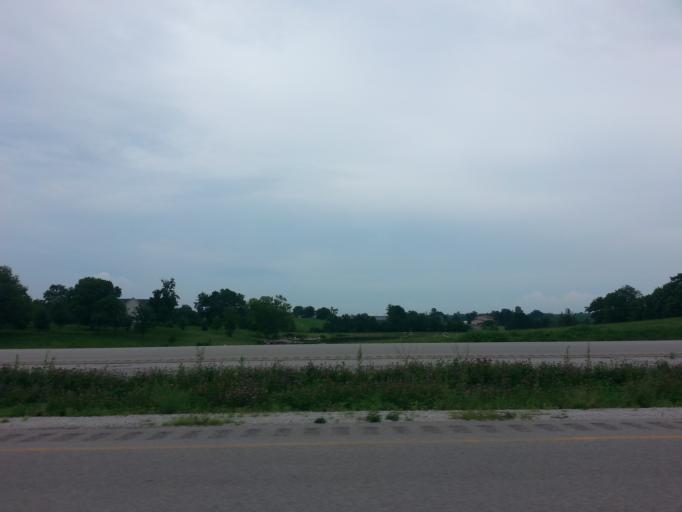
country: US
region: Ohio
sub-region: Brown County
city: Aberdeen
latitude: 38.6314
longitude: -83.8350
